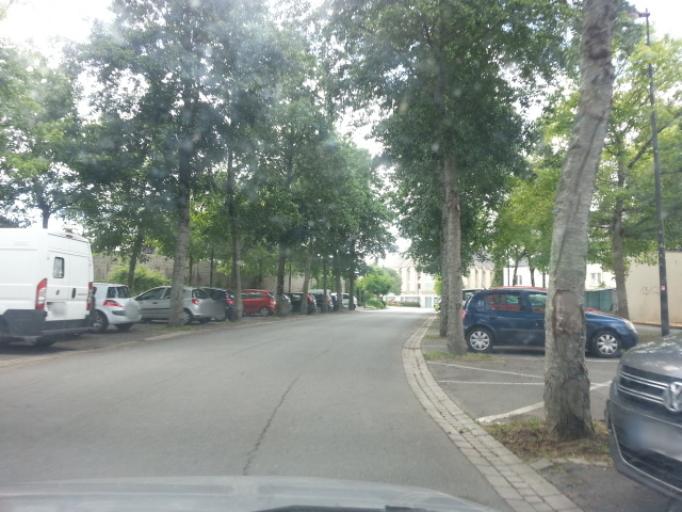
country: FR
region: Brittany
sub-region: Departement du Morbihan
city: Lanester
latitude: 47.7652
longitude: -3.3444
